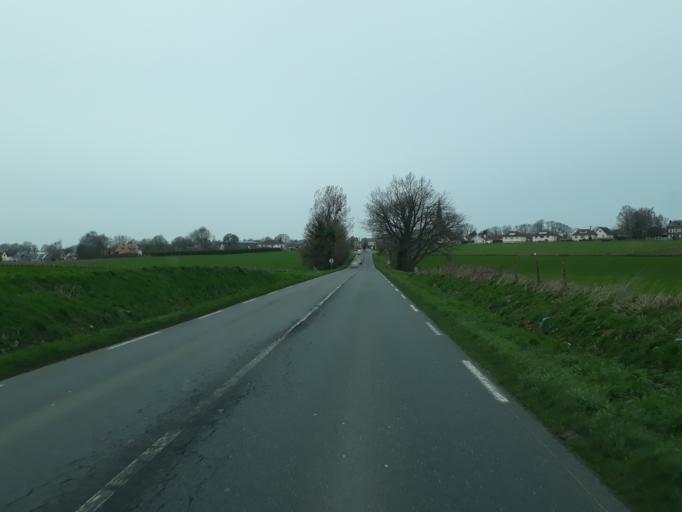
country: FR
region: Haute-Normandie
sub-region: Departement de la Seine-Maritime
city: Beuzeville-la-Grenier
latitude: 49.5884
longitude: 0.4335
